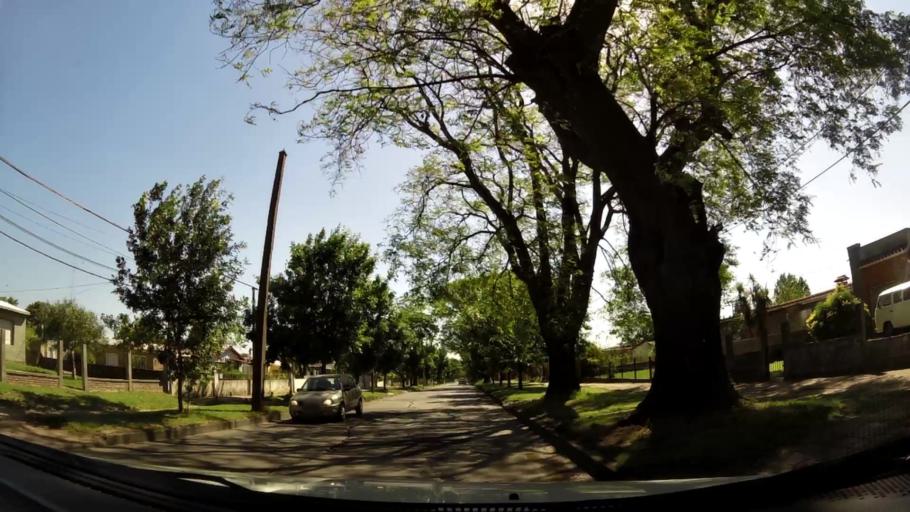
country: UY
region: Montevideo
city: Pajas Blancas
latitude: -34.8371
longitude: -56.2599
